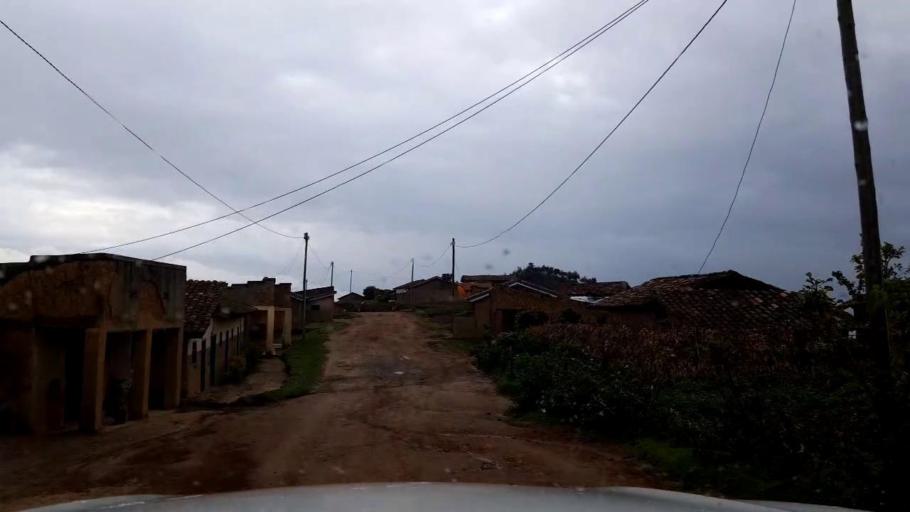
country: RW
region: Western Province
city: Kibuye
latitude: -2.0123
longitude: 29.4722
